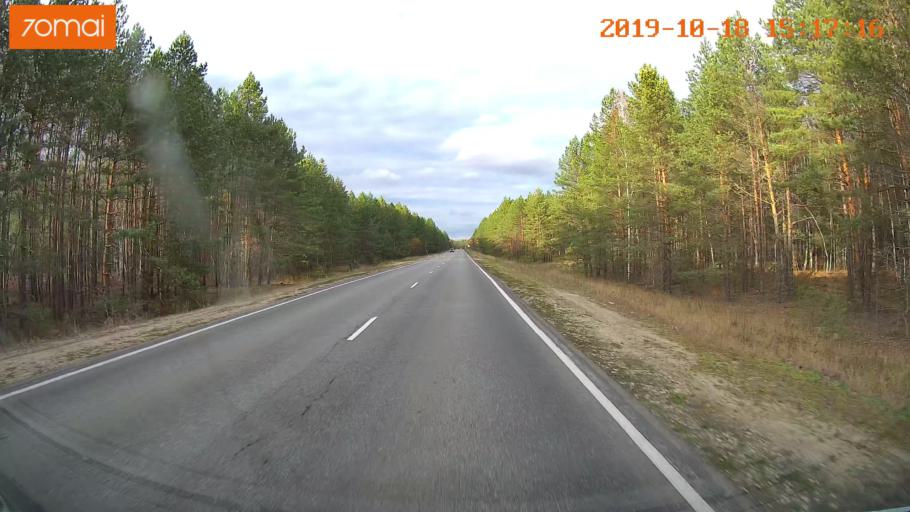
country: RU
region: Vladimir
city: Anopino
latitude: 55.6471
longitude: 40.7262
